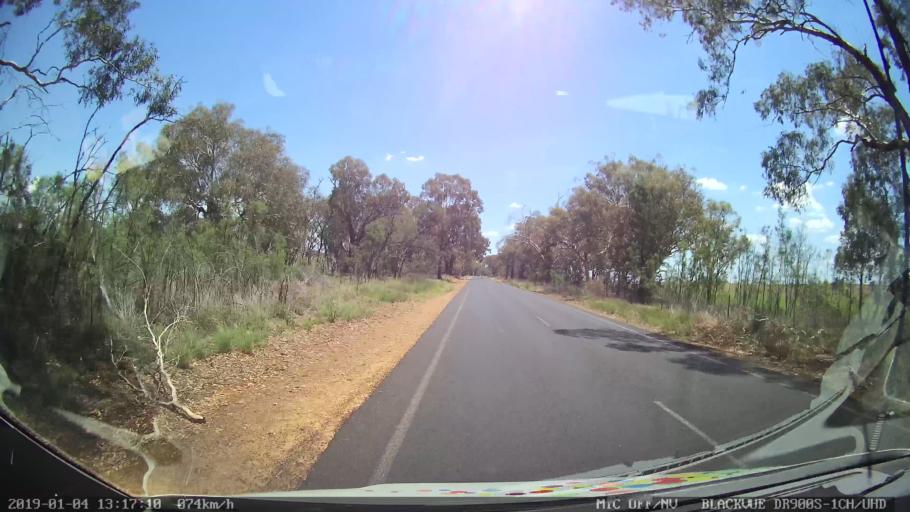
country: AU
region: New South Wales
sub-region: Wellington
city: Wellington
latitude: -32.7520
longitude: 148.6367
